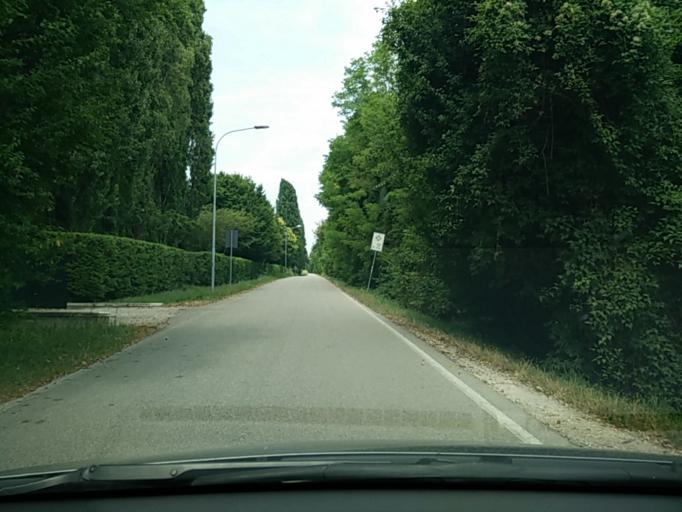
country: IT
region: Veneto
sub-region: Provincia di Treviso
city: Casier
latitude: 45.6485
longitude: 12.2906
